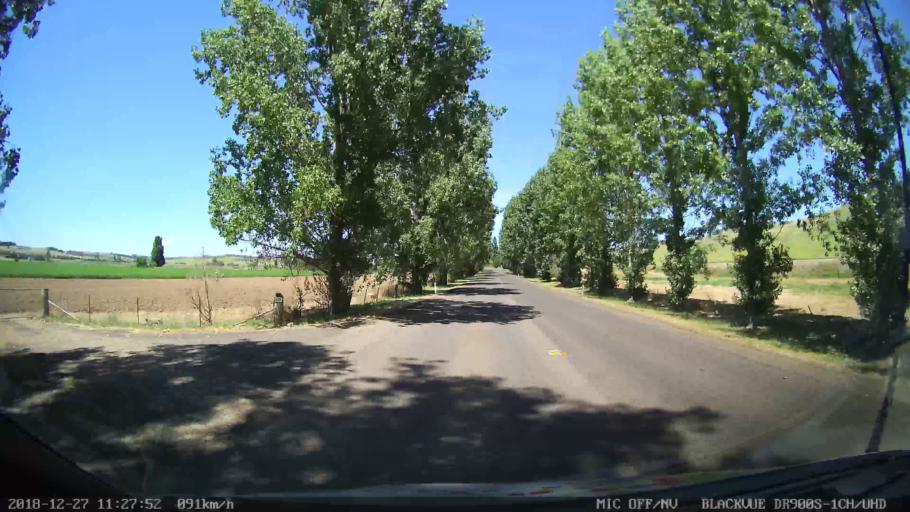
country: AU
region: New South Wales
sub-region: Bathurst Regional
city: Perthville
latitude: -33.4701
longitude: 149.5673
